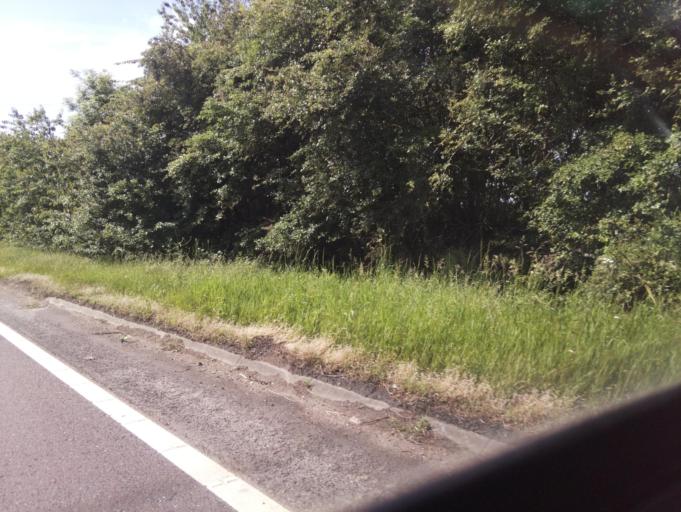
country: GB
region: England
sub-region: Lincolnshire
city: Skellingthorpe
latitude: 53.1810
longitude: -0.6262
